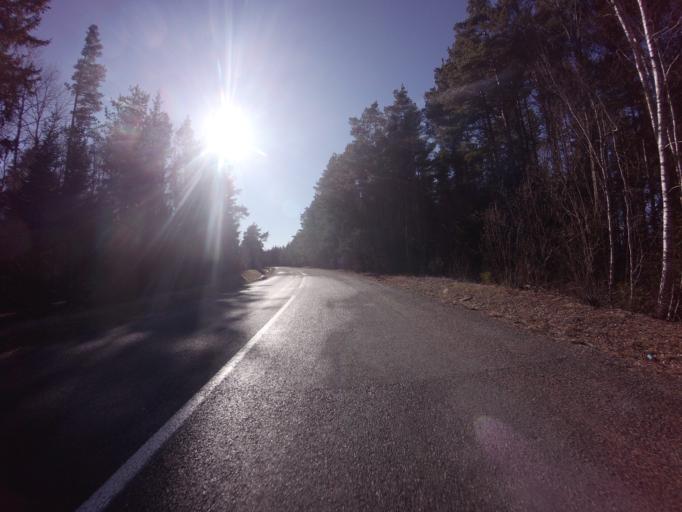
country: EE
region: Saare
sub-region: Kuressaare linn
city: Kuressaare
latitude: 58.5039
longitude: 22.3086
